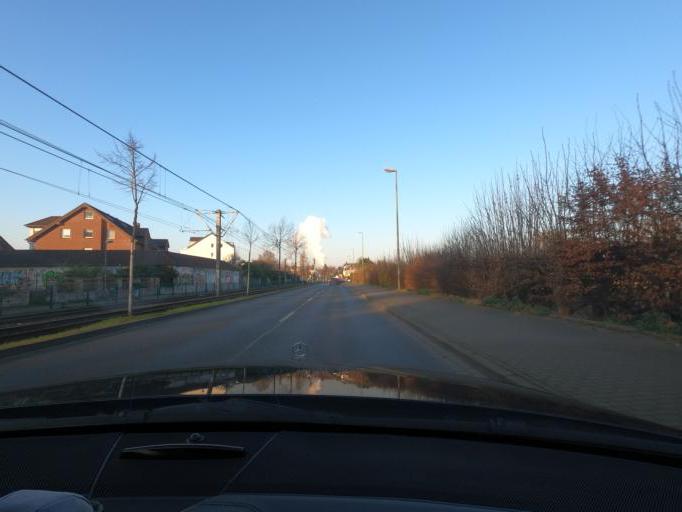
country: DE
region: North Rhine-Westphalia
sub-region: Regierungsbezirk Arnsberg
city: Dortmund
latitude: 51.5778
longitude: 7.4628
